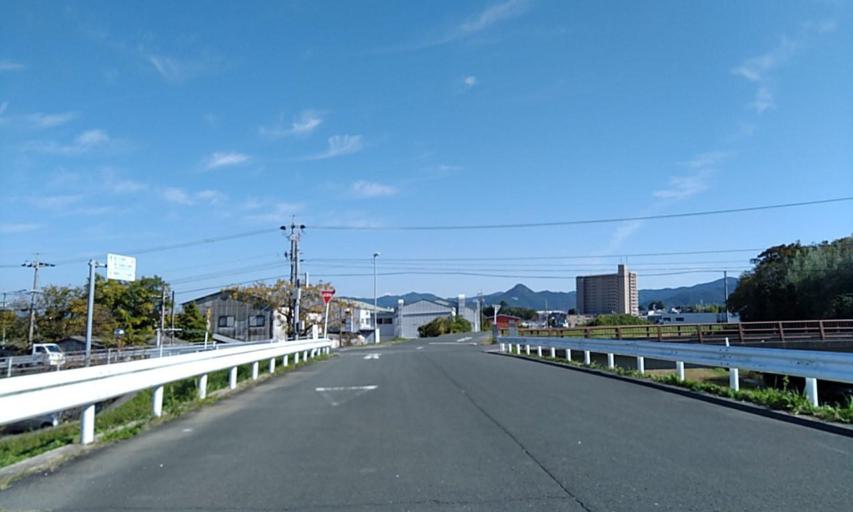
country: JP
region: Aichi
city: Toyohashi
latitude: 34.7724
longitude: 137.4002
